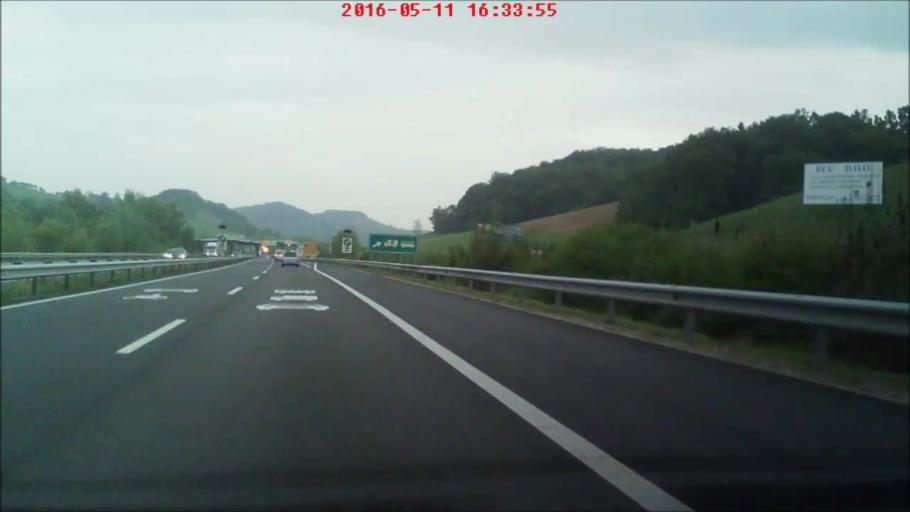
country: SI
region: Pesnica
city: Pesnica pri Mariboru
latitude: 46.6193
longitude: 15.6589
